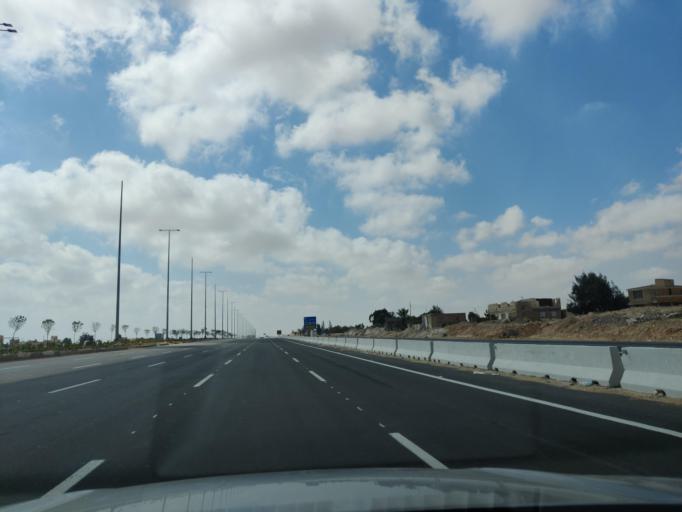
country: EG
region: Muhafazat Matruh
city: Al `Alamayn
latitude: 30.9332
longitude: 28.7895
